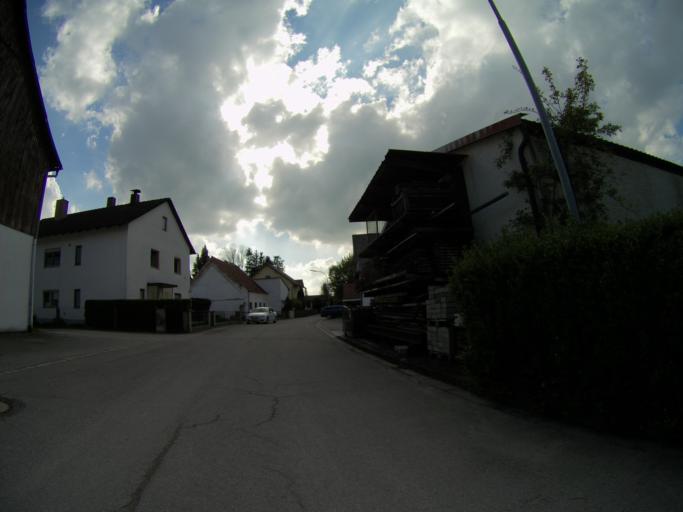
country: DE
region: Bavaria
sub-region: Upper Bavaria
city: Marzling
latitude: 48.3790
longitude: 11.7760
